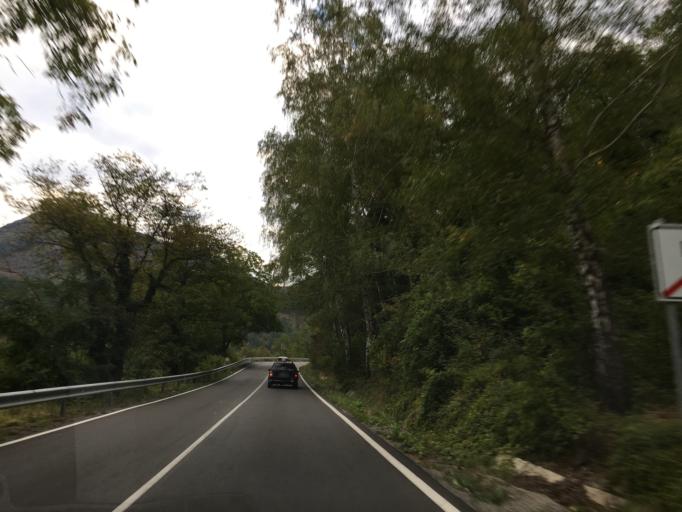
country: BG
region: Sofiya
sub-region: Obshtina Svoge
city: Bov
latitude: 43.0171
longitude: 23.3515
